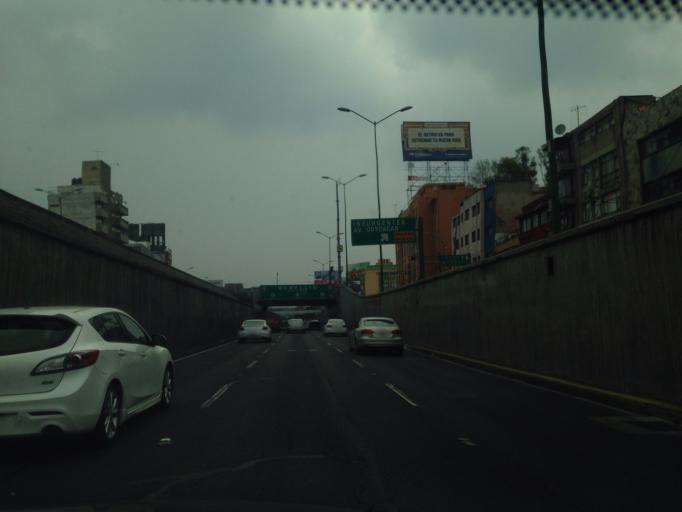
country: MX
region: Mexico City
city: Benito Juarez
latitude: 19.4028
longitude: -99.1615
